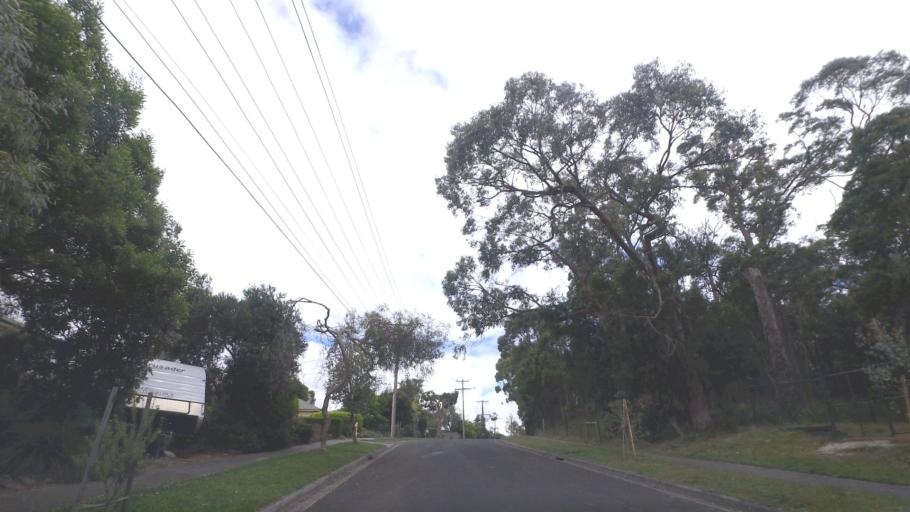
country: AU
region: Victoria
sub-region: Maroondah
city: Croydon South
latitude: -37.7951
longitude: 145.2711
